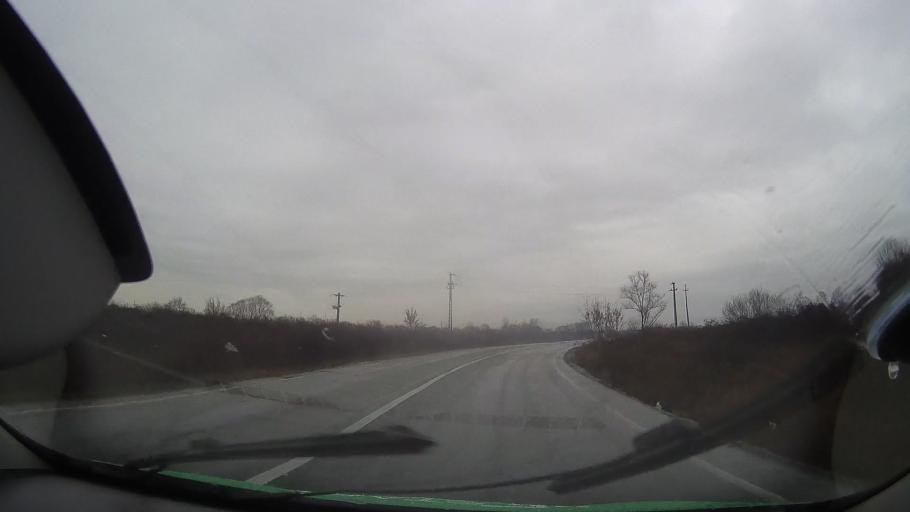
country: RO
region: Bihor
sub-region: Comuna Sambata
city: Sambata
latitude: 46.7818
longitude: 22.1880
